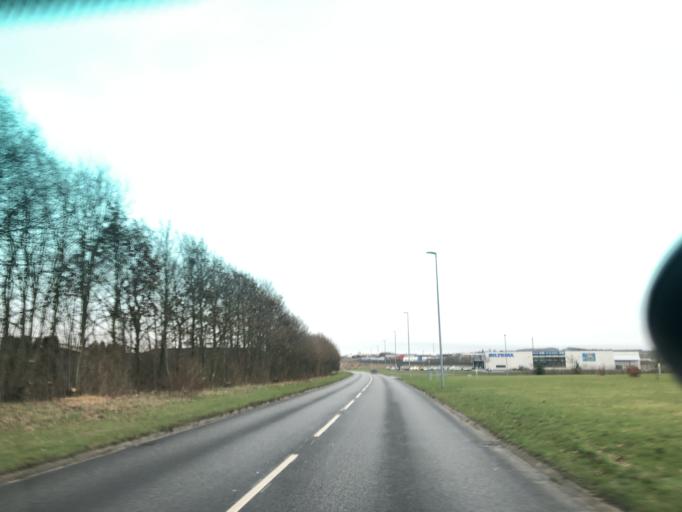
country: DK
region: Central Jutland
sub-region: Randers Kommune
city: Randers
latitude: 56.4259
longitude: 10.0634
